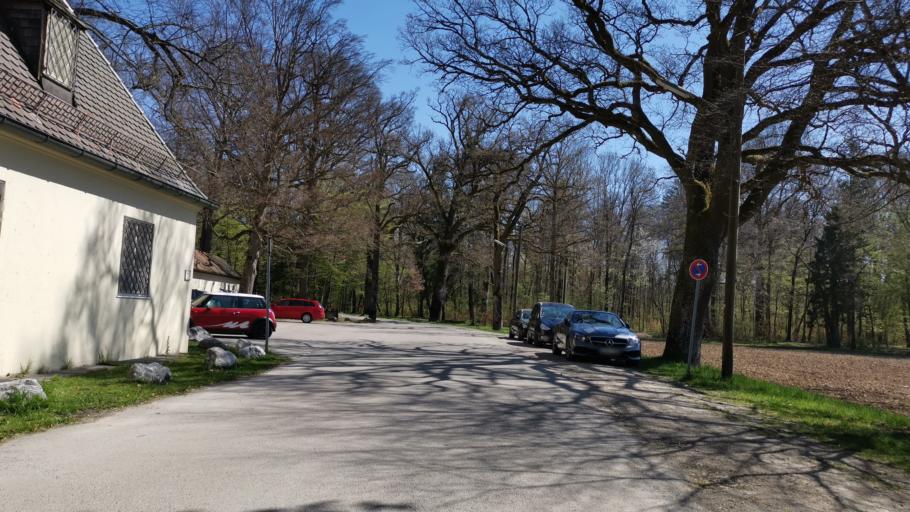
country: DE
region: Bavaria
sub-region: Upper Bavaria
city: Pullach im Isartal
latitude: 48.0679
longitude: 11.5133
